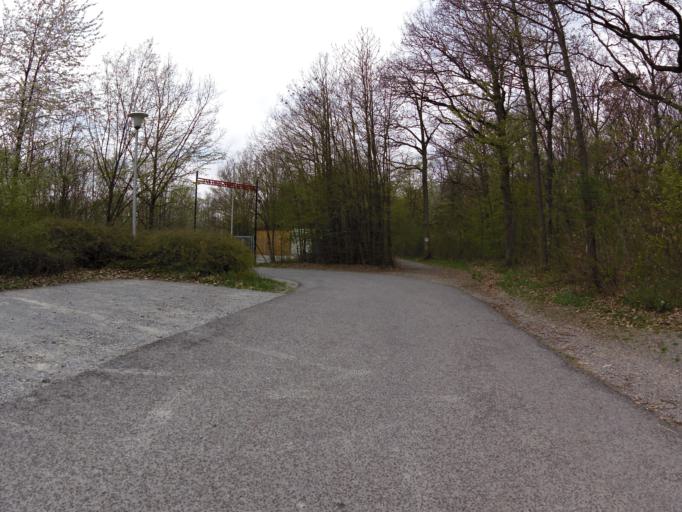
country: DE
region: Bavaria
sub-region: Regierungsbezirk Unterfranken
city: Rottendorf
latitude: 49.7984
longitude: 10.0166
